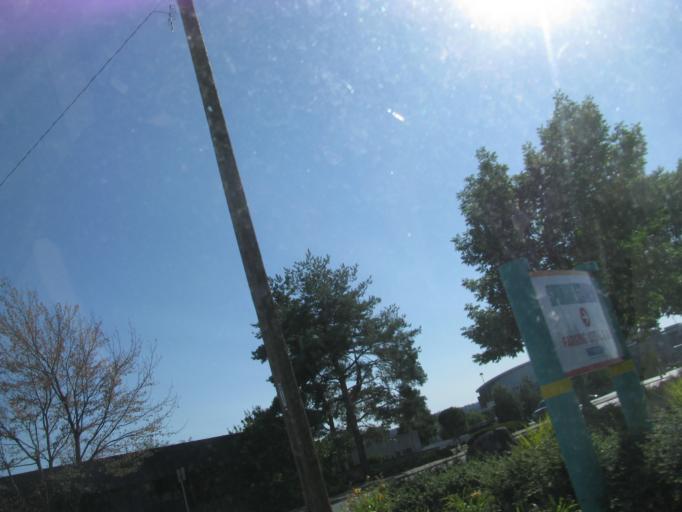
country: US
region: Washington
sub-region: Spokane County
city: Spokane
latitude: 47.6676
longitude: -117.4174
